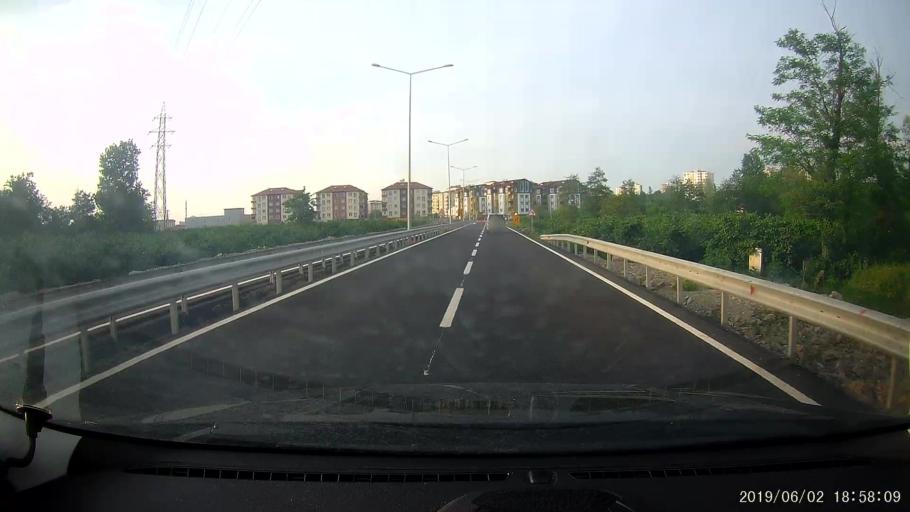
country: TR
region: Ordu
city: Ordu
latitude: 40.9589
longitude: 37.9073
